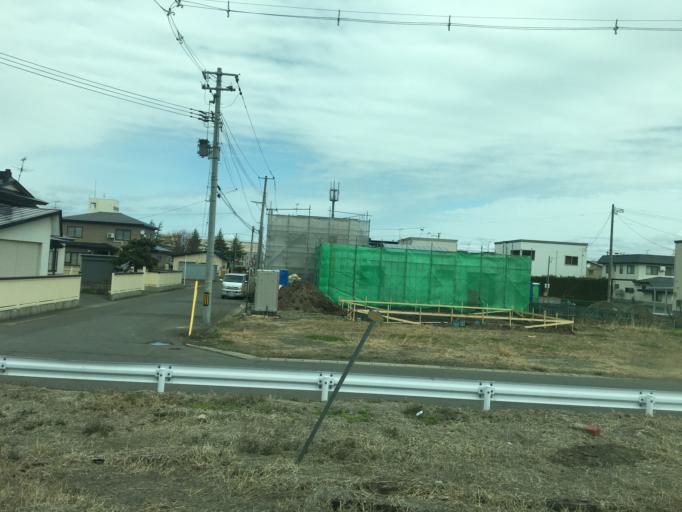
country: JP
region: Aomori
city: Hirosaki
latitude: 40.6534
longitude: 140.5005
